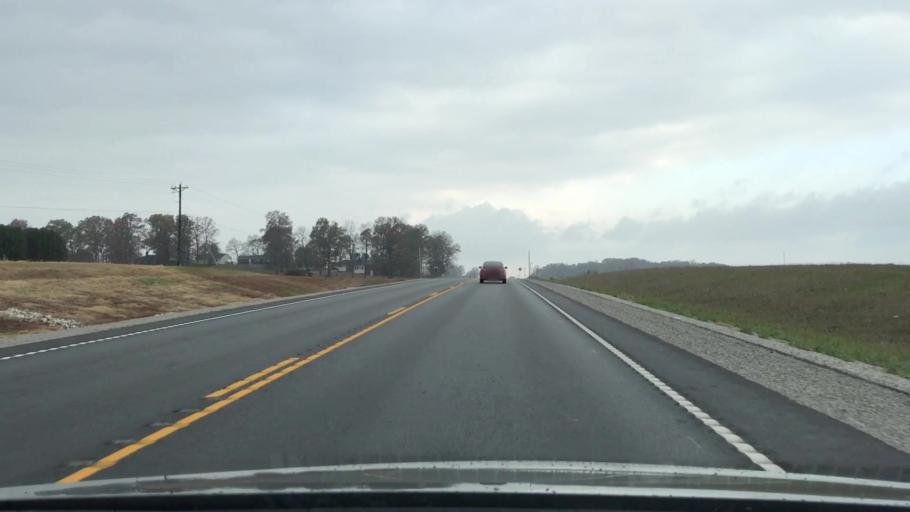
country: US
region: Kentucky
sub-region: Simpson County
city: Franklin
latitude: 36.7089
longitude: -86.4822
